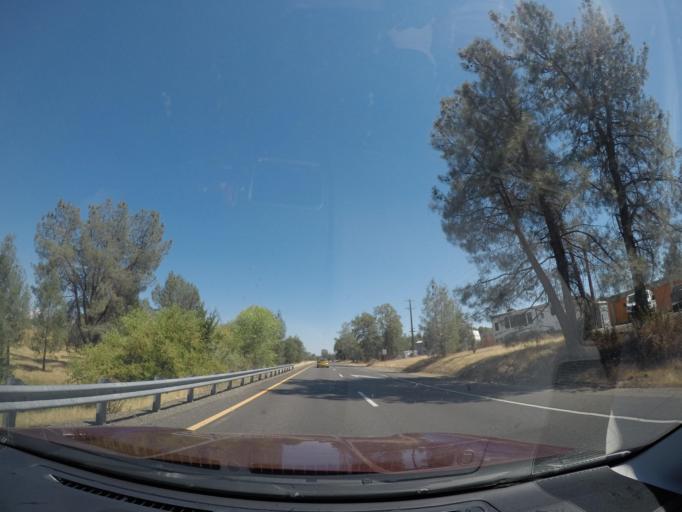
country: US
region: California
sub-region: Shasta County
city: Redding
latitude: 40.6110
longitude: -122.3652
